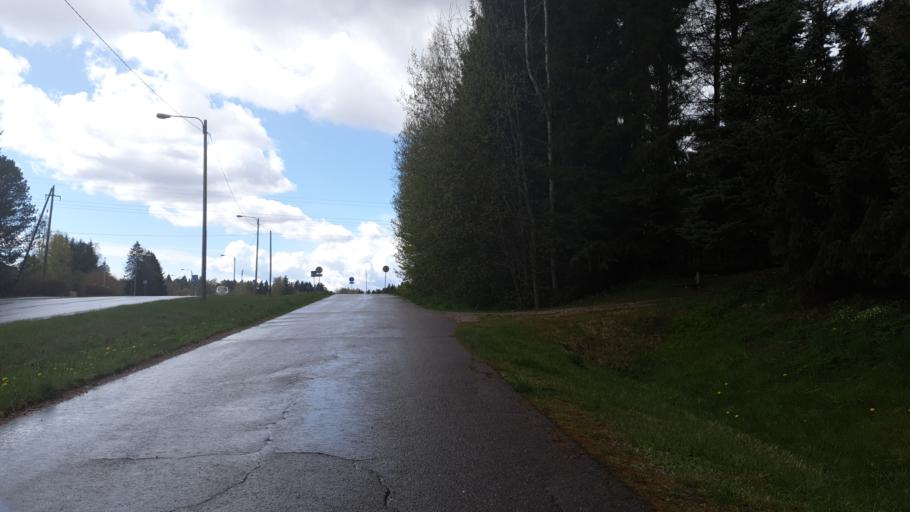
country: FI
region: Uusimaa
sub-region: Helsinki
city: Tuusula
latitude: 60.3531
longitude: 24.9467
